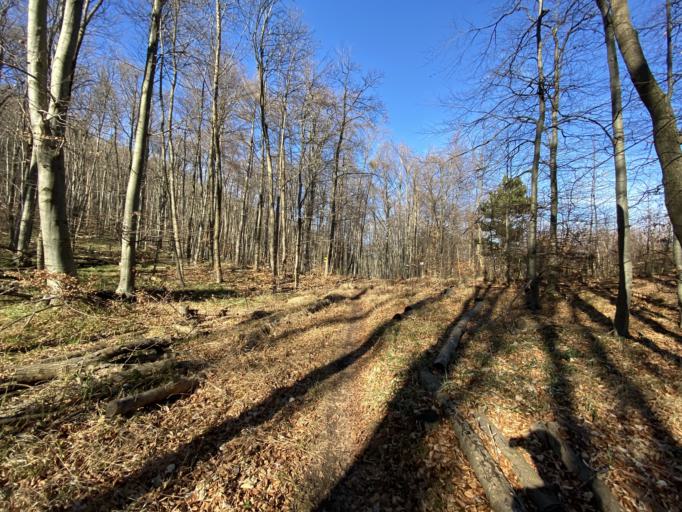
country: AT
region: Lower Austria
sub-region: Politischer Bezirk Baden
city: Heiligenkreuz
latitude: 48.0043
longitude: 16.1431
